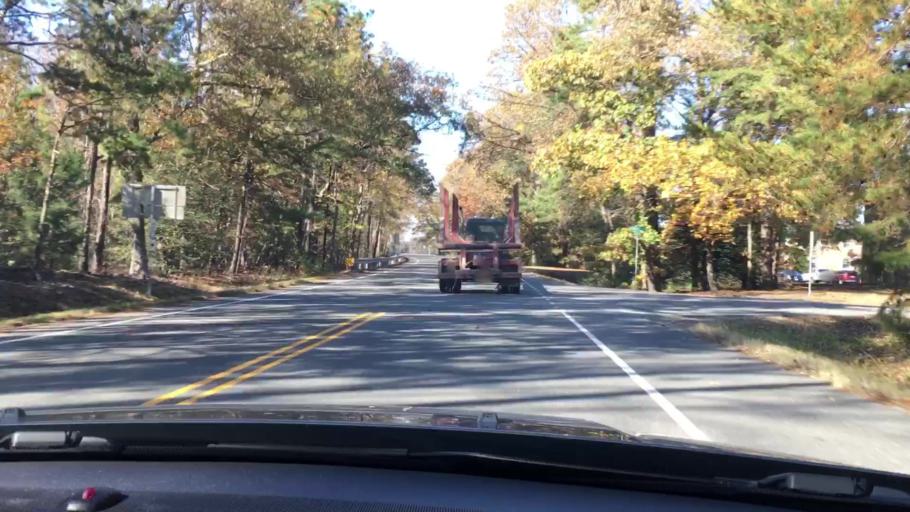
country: US
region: Virginia
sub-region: King William County
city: Central Garage
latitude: 37.7595
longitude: -77.1449
